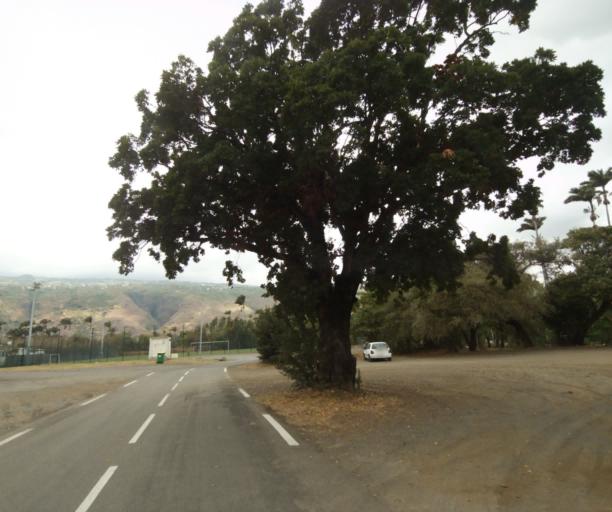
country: RE
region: Reunion
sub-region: Reunion
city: Saint-Paul
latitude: -20.9892
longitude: 55.2990
